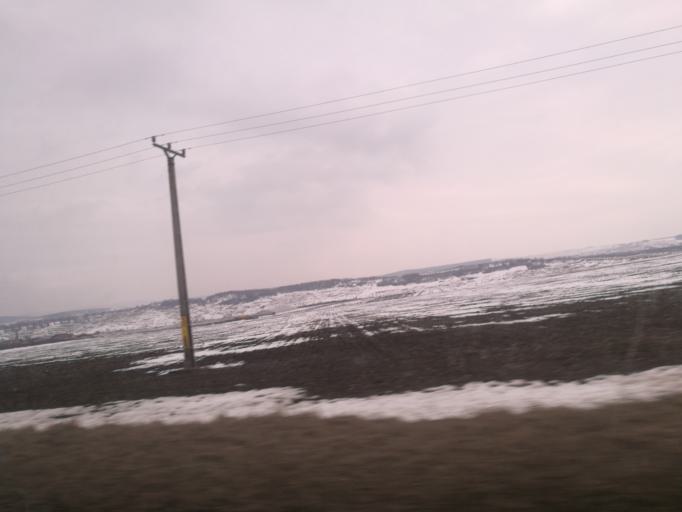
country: RO
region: Iasi
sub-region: Comuna Targu Frumos
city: Targu Frumos
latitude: 47.2051
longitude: 26.9915
